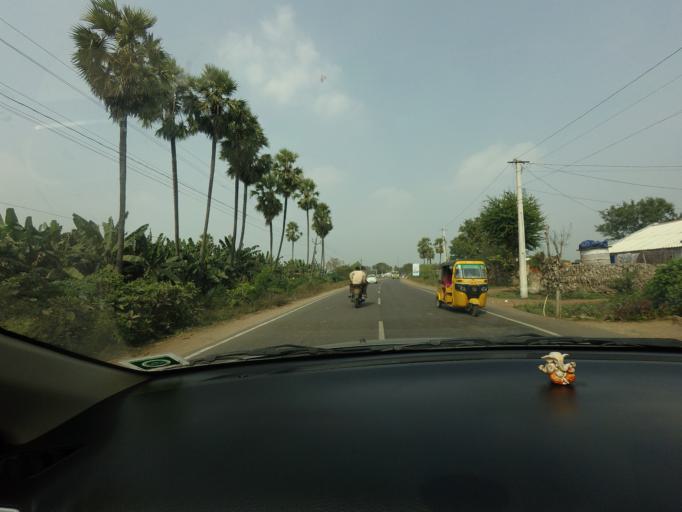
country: IN
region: Andhra Pradesh
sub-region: Krishna
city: Kankipadu
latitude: 16.4498
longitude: 80.7707
